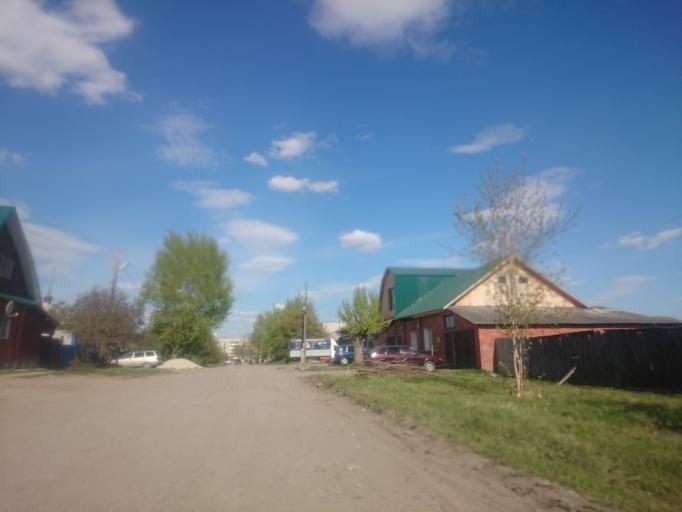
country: RU
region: Sverdlovsk
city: Irbit
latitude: 57.6694
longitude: 63.0658
